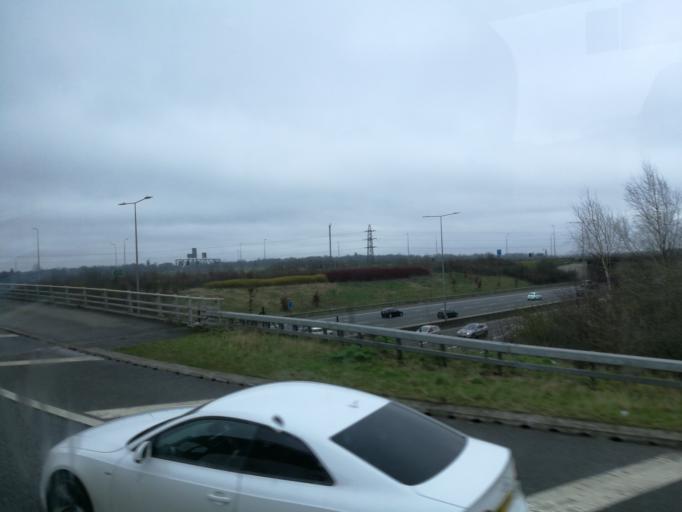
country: GB
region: England
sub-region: Luton
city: Luton
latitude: 51.8544
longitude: -0.4247
